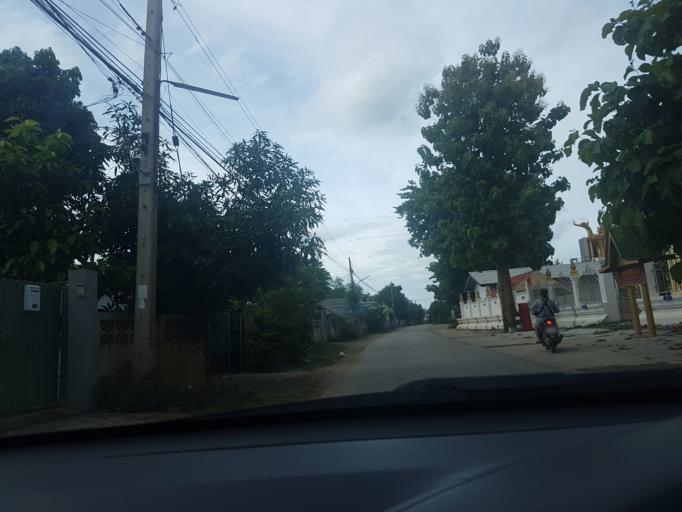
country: TH
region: Lampang
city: Ko Kha
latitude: 18.2147
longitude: 99.4134
